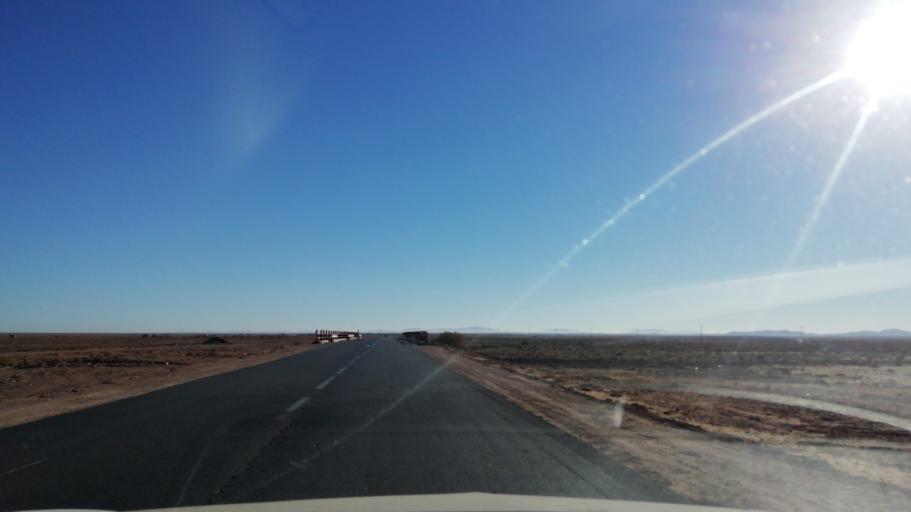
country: DZ
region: El Bayadh
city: El Bayadh
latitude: 33.8573
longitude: 0.5821
